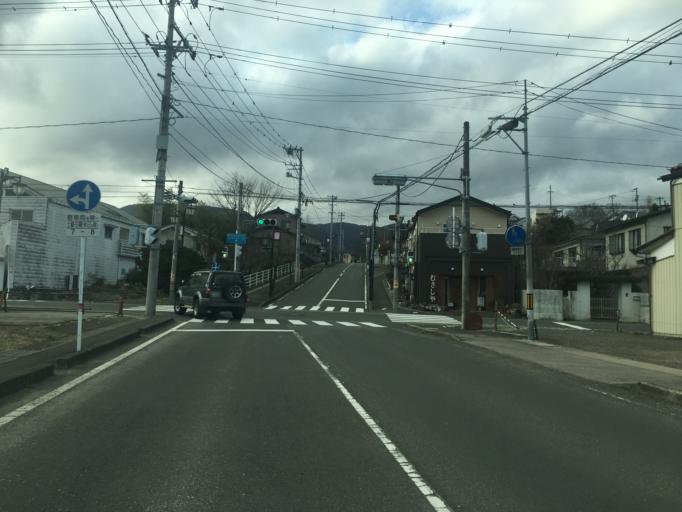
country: JP
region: Fukushima
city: Hobaramachi
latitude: 37.8766
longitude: 140.5460
